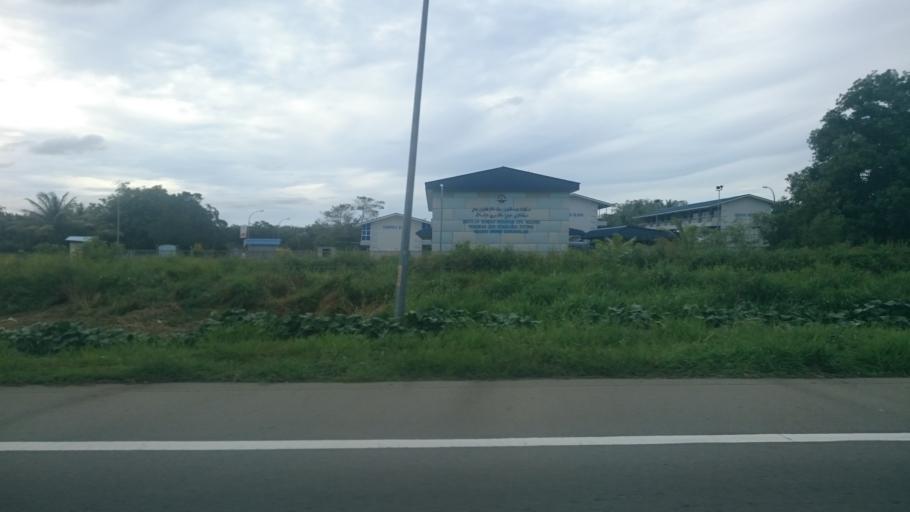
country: BN
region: Tutong
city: Tutong
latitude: 4.8012
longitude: 114.6489
